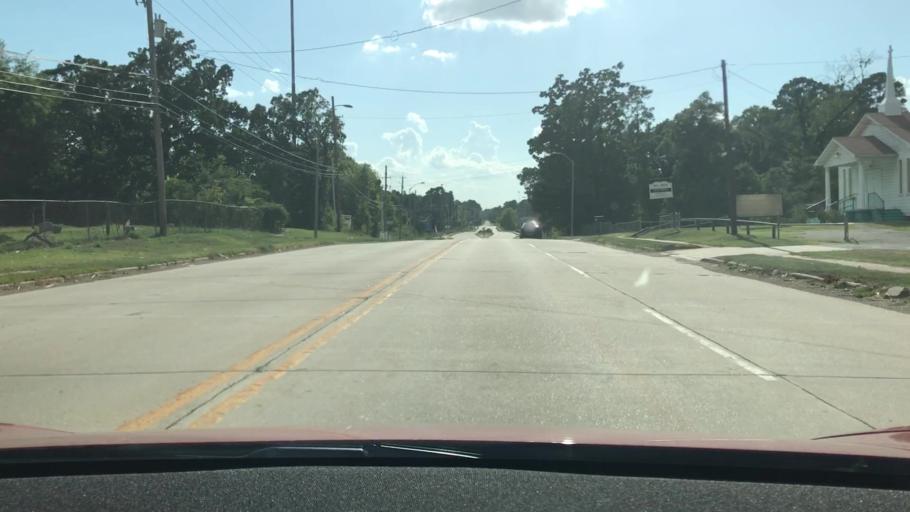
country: US
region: Louisiana
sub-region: Bossier Parish
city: Bossier City
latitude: 32.4130
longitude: -93.7708
